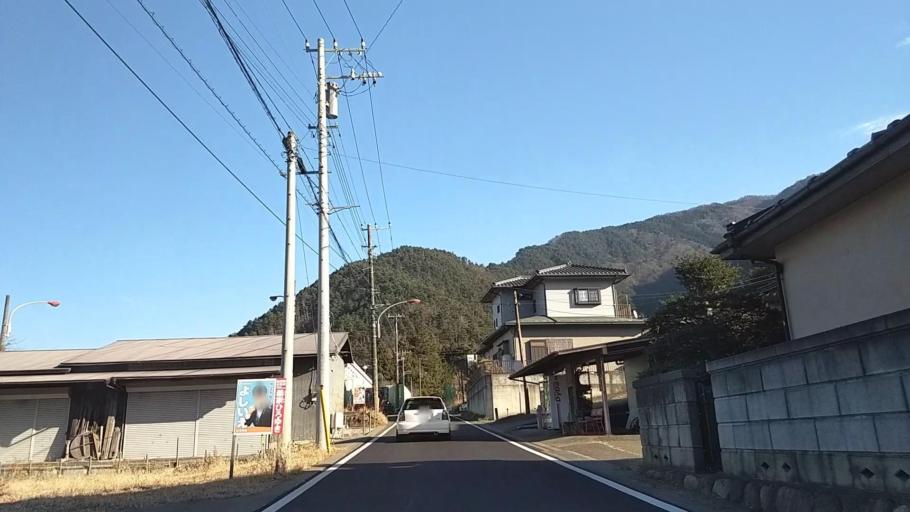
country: JP
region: Yamanashi
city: Uenohara
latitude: 35.5435
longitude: 139.1336
